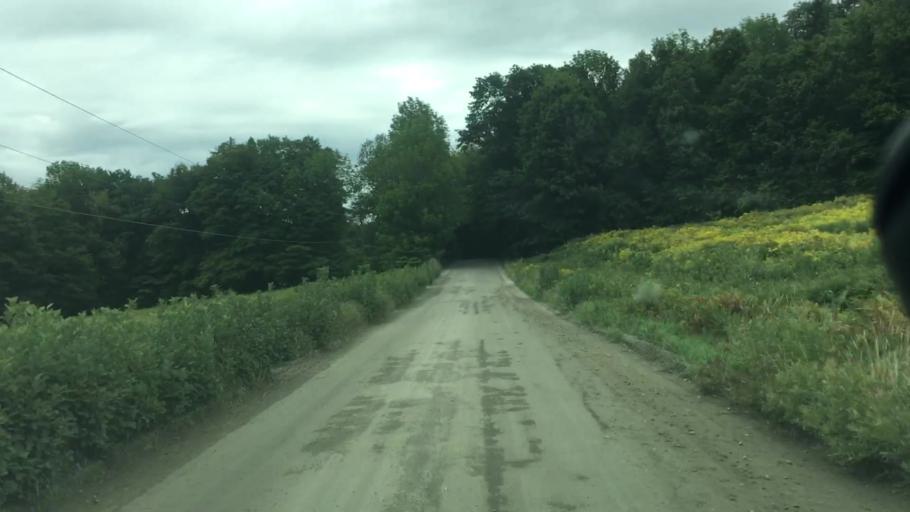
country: US
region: Vermont
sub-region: Windham County
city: Dover
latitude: 42.8557
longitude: -72.7792
